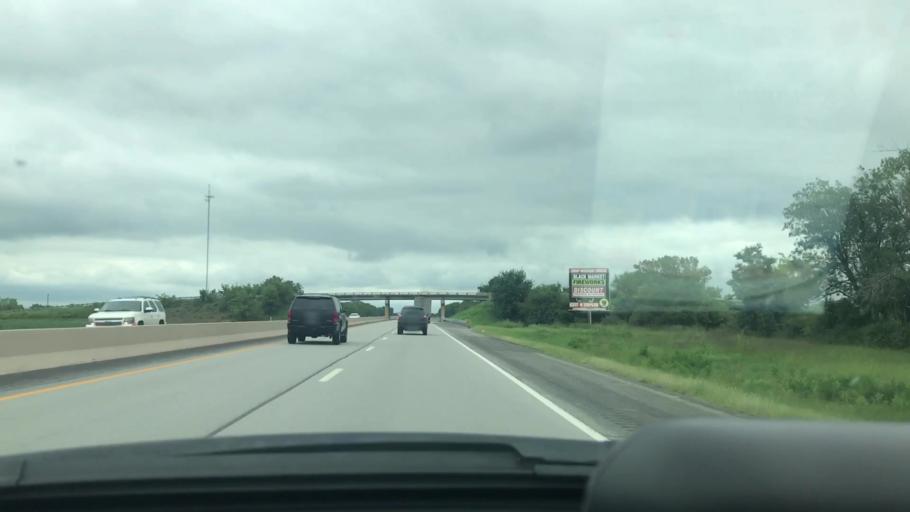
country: US
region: Oklahoma
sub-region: Ottawa County
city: Commerce
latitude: 36.9109
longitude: -94.7904
